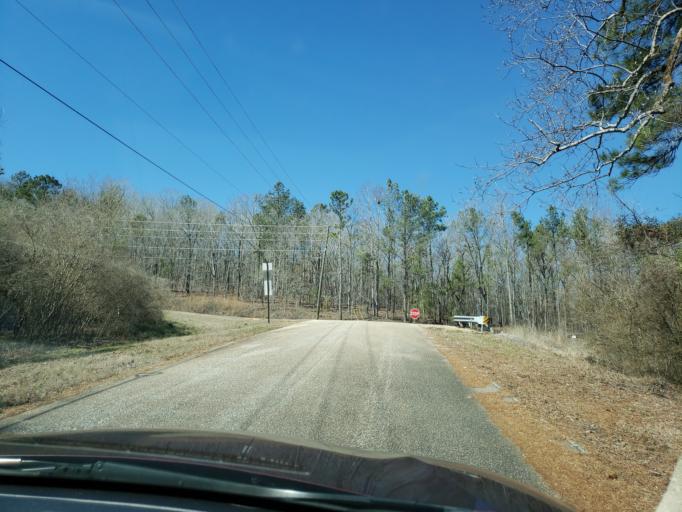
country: US
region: Alabama
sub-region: Elmore County
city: Eclectic
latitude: 32.6741
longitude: -85.9117
